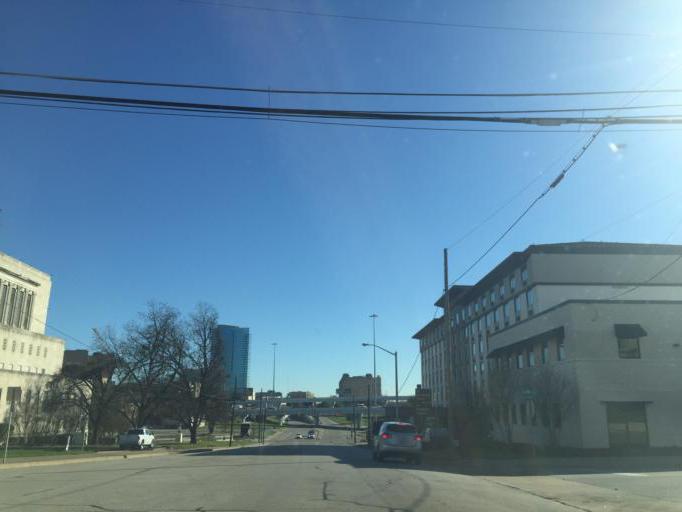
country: US
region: Texas
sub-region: Tarrant County
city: Fort Worth
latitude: 32.7467
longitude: -97.3393
